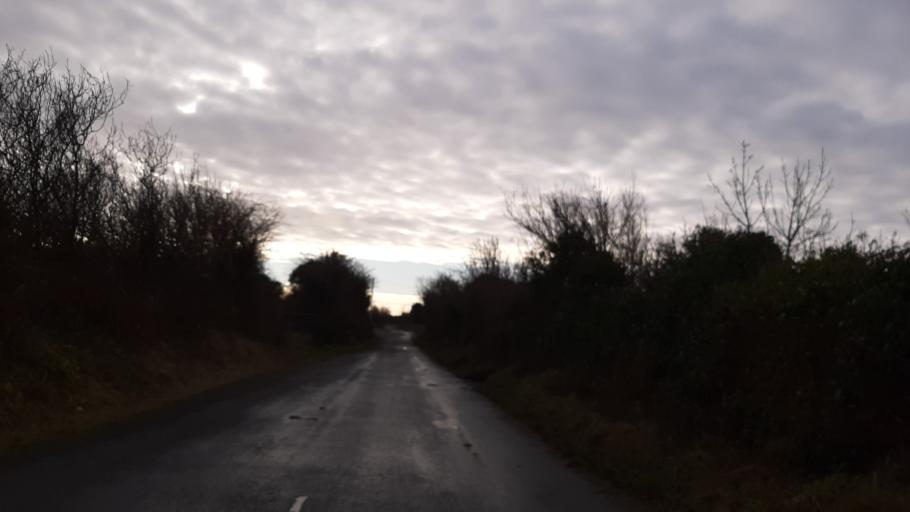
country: IE
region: Connaught
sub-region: County Galway
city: Gaillimh
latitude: 53.3143
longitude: -9.0664
